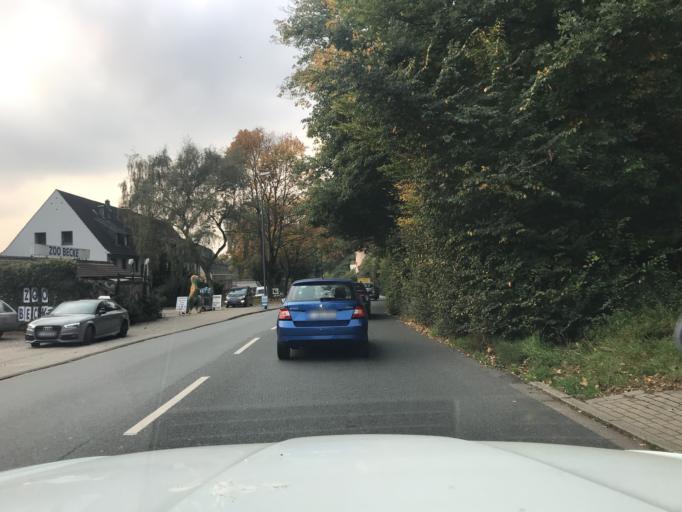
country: DE
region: North Rhine-Westphalia
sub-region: Regierungsbezirk Dusseldorf
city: Velbert
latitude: 51.3887
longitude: 7.0152
